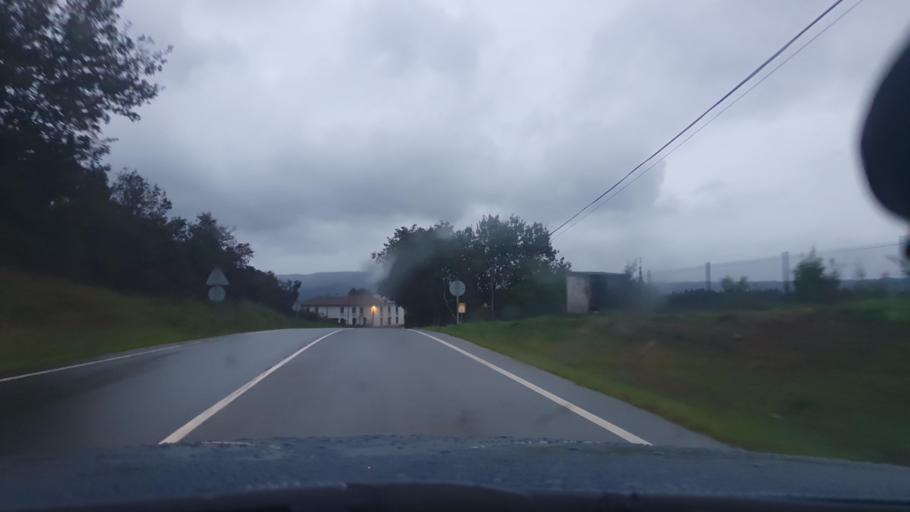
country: ES
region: Galicia
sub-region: Provincia da Coruna
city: Santiago de Compostela
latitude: 42.8416
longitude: -8.5974
